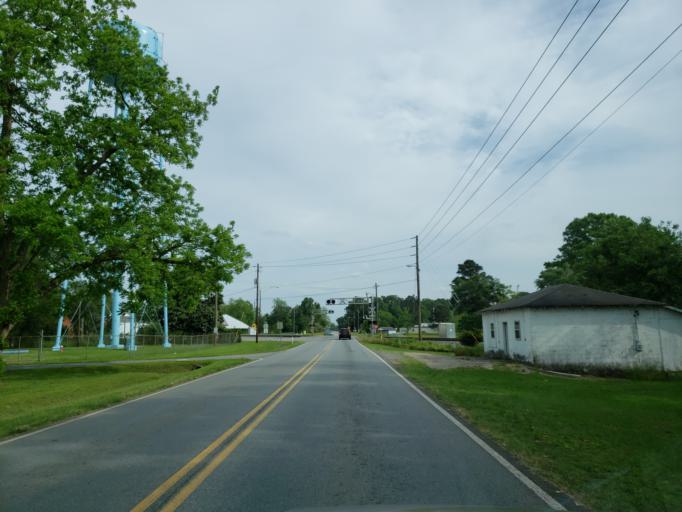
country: US
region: Georgia
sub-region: Dooly County
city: Vienna
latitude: 32.1483
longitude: -83.8784
